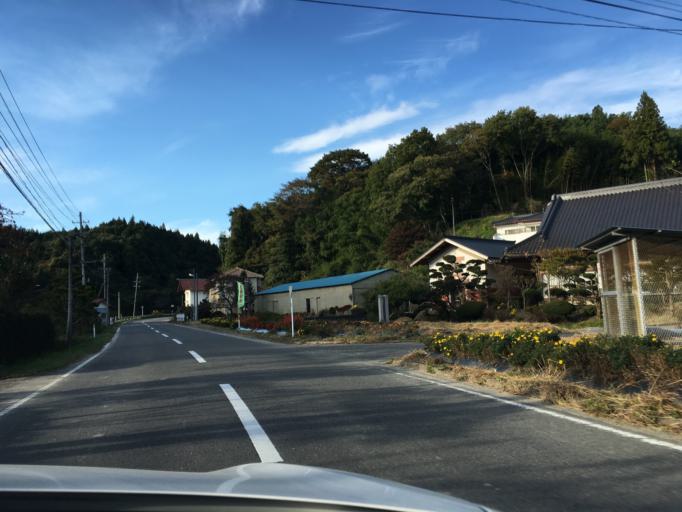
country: JP
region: Fukushima
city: Ishikawa
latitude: 37.2094
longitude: 140.5821
